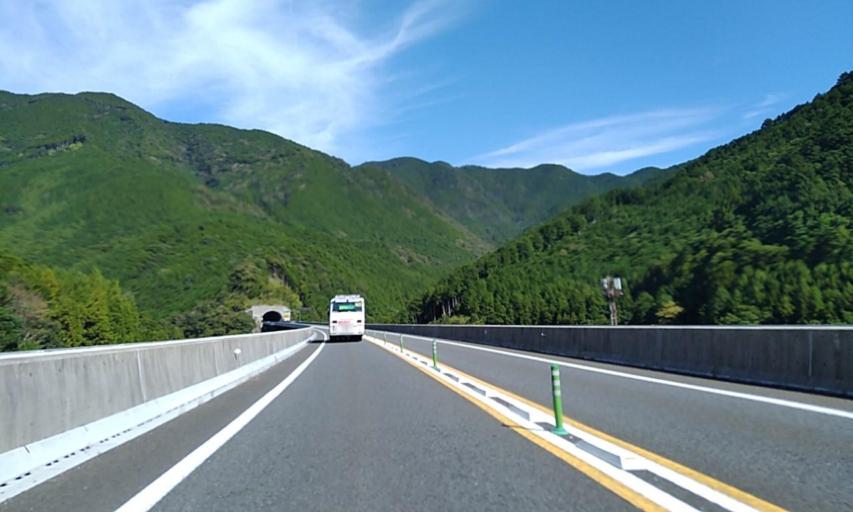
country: JP
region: Mie
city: Owase
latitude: 33.9423
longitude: 136.1526
